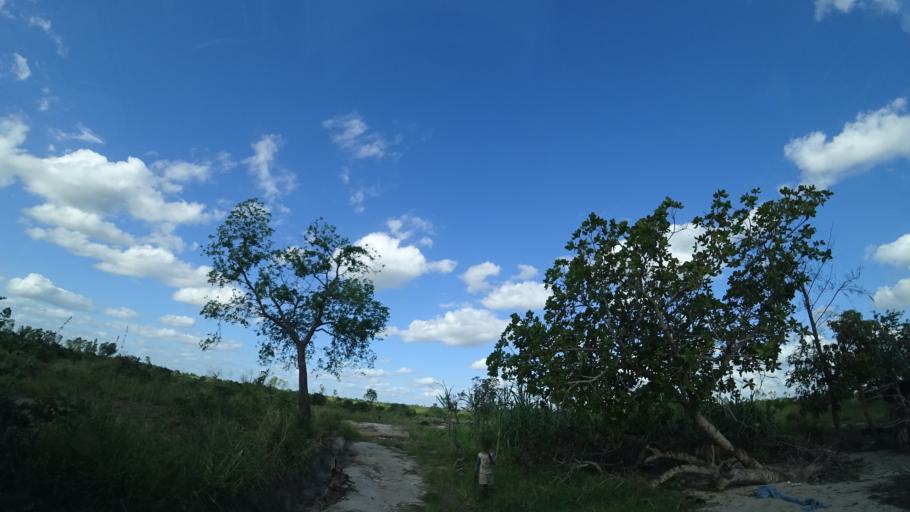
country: MZ
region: Sofala
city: Dondo
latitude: -19.4259
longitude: 34.7073
